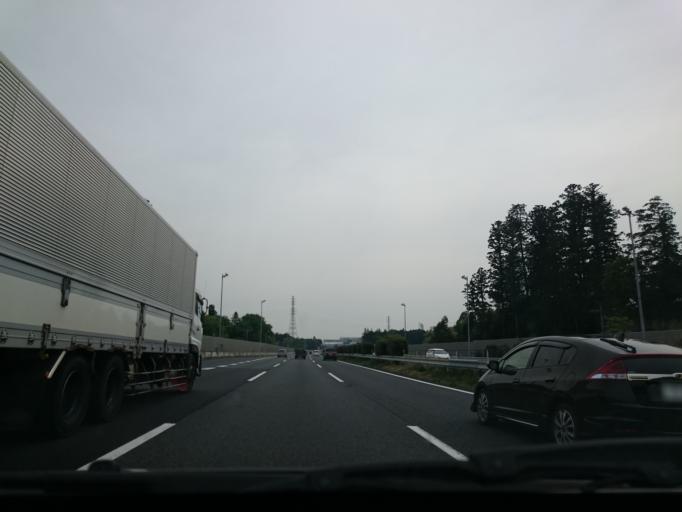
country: JP
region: Tochigi
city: Utsunomiya-shi
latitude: 36.5970
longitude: 139.8427
